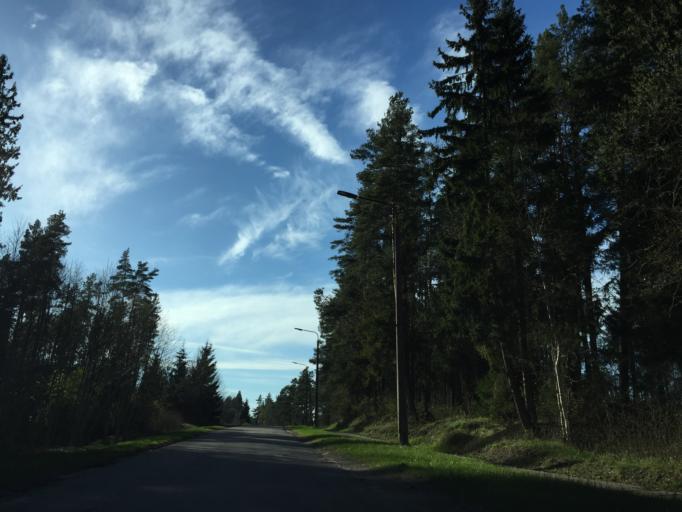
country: LV
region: Valkas Rajons
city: Valka
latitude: 57.7880
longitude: 25.9929
